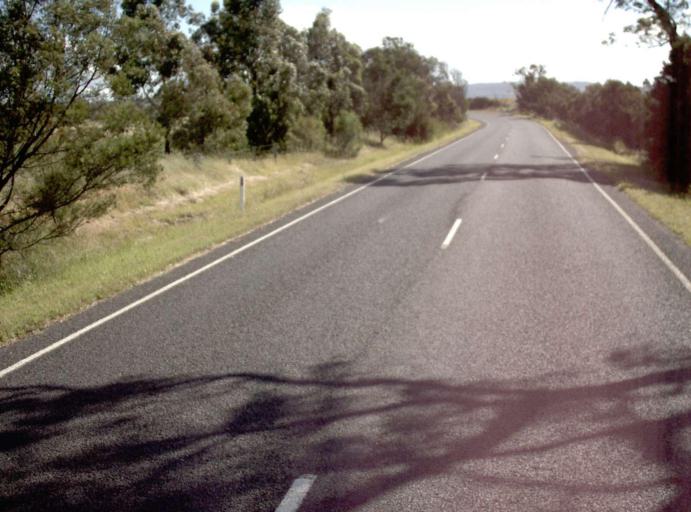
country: AU
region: Victoria
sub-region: Latrobe
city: Morwell
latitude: -38.1704
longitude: 146.4088
